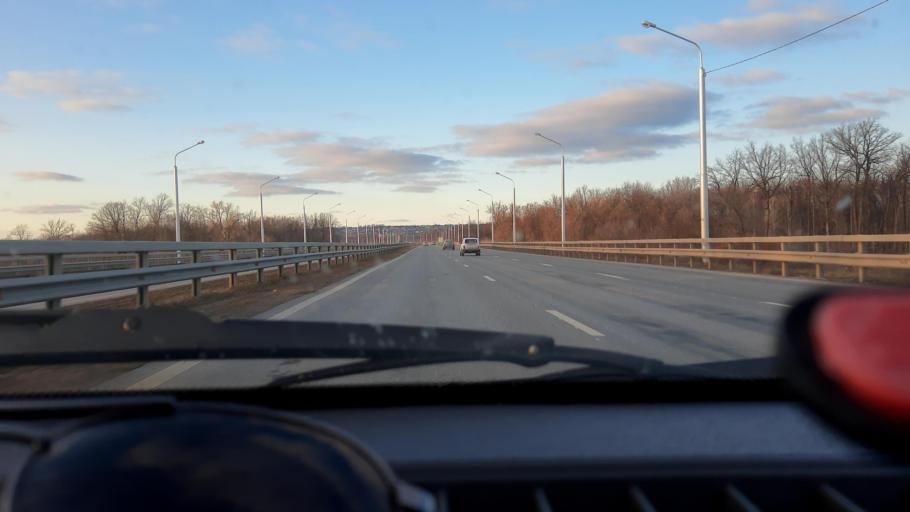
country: RU
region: Bashkortostan
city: Mikhaylovka
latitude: 54.7875
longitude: 55.9074
